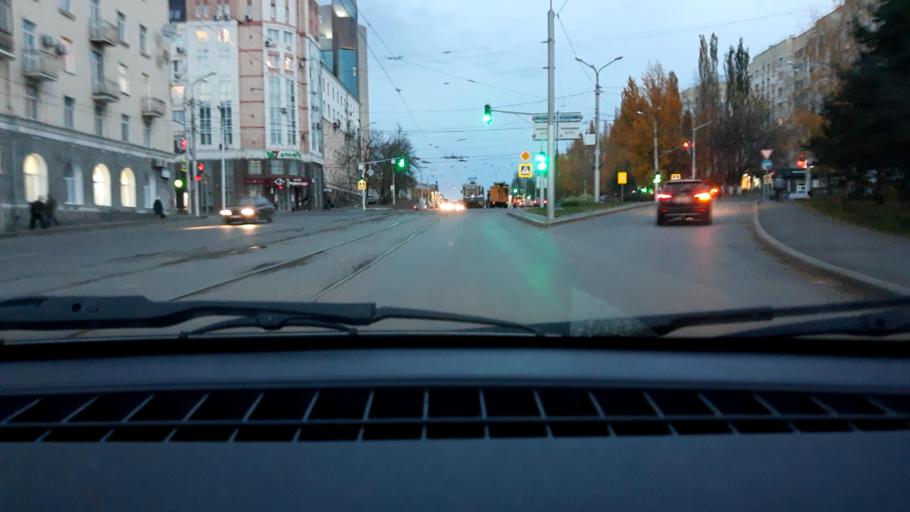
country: RU
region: Bashkortostan
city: Ufa
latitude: 54.7369
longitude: 55.9448
